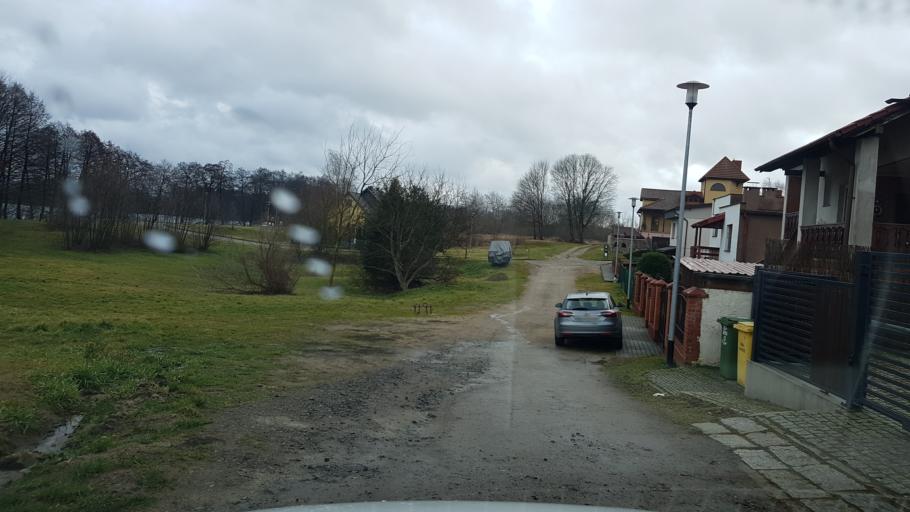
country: PL
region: West Pomeranian Voivodeship
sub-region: Powiat drawski
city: Czaplinek
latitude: 53.5515
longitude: 16.2463
